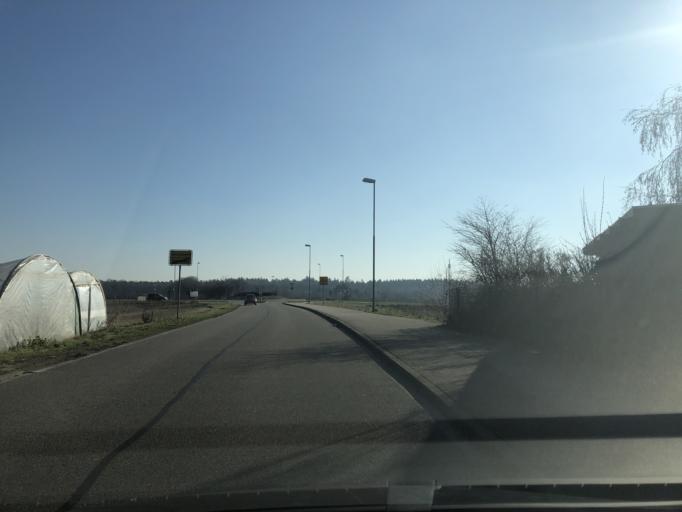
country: DE
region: Baden-Wuerttemberg
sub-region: Karlsruhe Region
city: Eggenstein-Leopoldshafen
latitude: 49.0789
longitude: 8.4015
